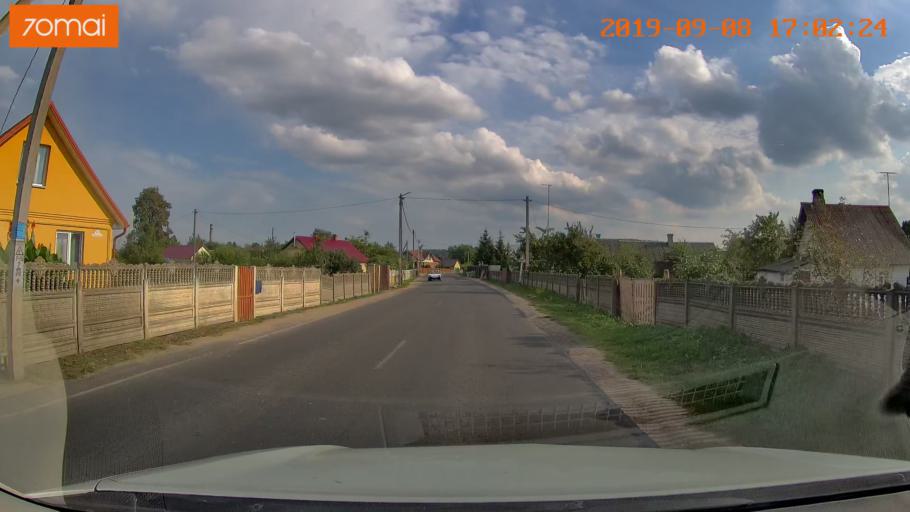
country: BY
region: Grodnenskaya
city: Hrodna
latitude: 53.7039
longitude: 23.9389
